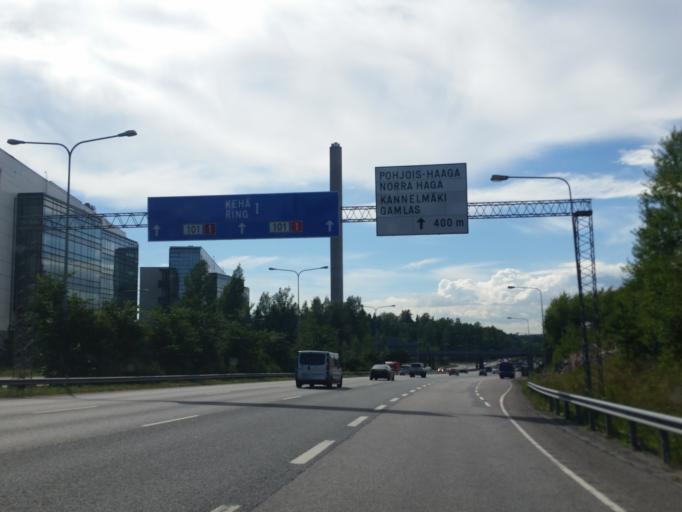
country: FI
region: Uusimaa
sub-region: Helsinki
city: Teekkarikylae
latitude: 60.2348
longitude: 24.8953
